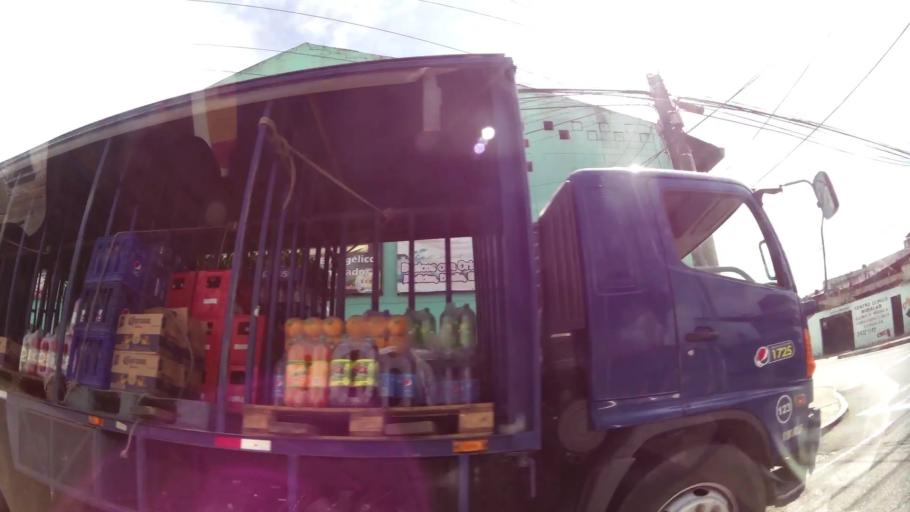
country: GT
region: Guatemala
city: Mixco
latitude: 14.6536
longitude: -90.5845
